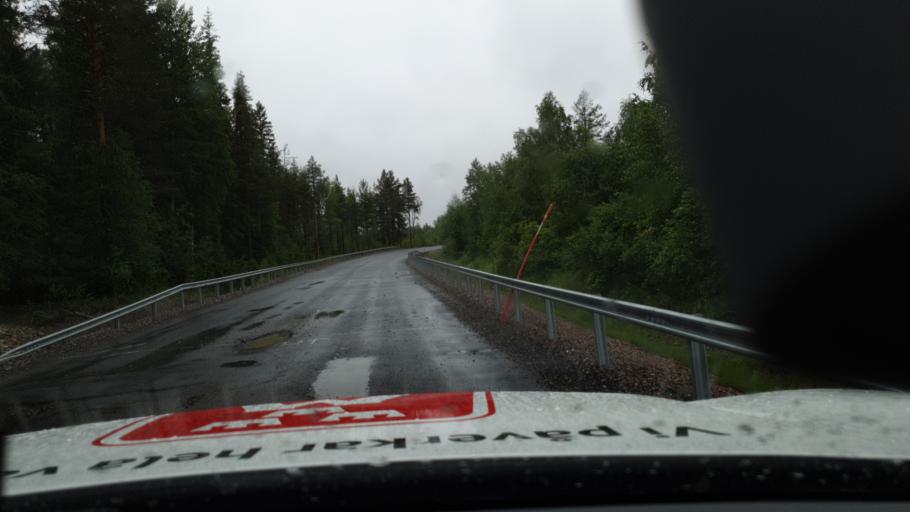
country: SE
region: Norrbotten
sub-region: Overtornea Kommun
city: OEvertornea
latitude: 66.5491
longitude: 23.3434
